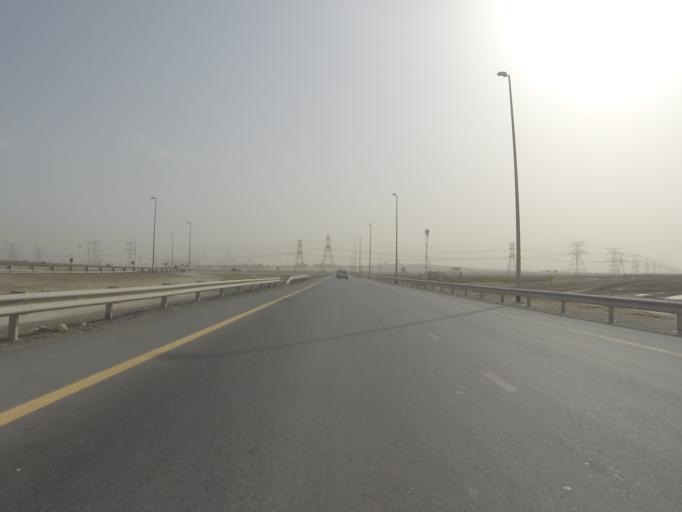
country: AE
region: Dubai
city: Dubai
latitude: 25.0144
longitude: 55.0997
